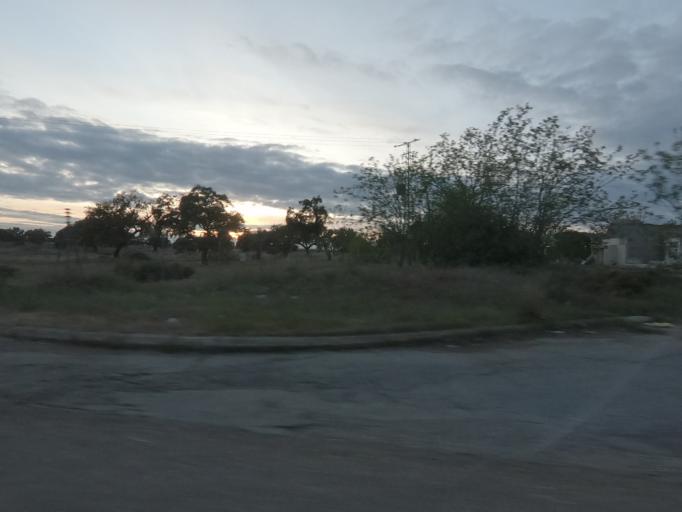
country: ES
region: Extremadura
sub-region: Provincia de Badajoz
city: Villar del Rey
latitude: 38.9931
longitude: -6.8726
